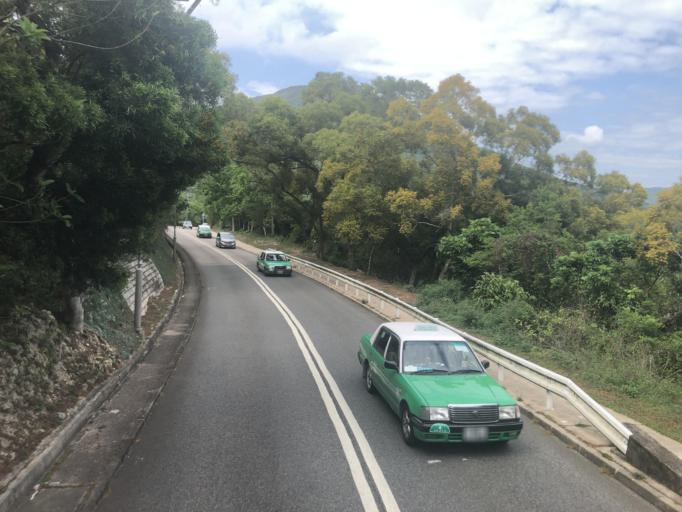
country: HK
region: Sai Kung
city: Sai Kung
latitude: 22.3882
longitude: 114.3074
